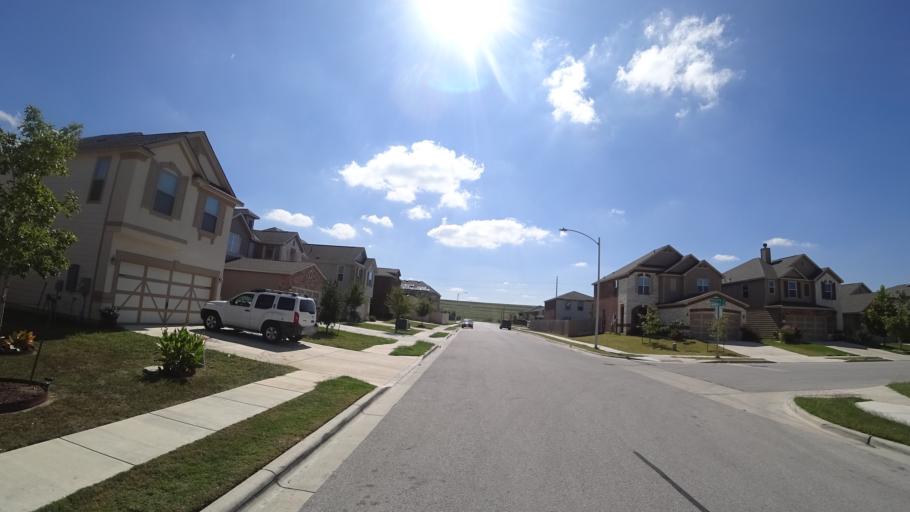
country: US
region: Texas
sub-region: Travis County
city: Manor
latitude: 30.3473
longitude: -97.6194
